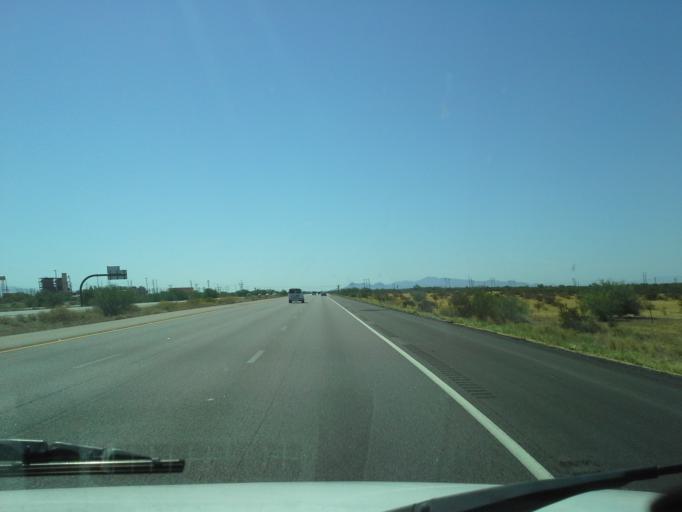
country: US
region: Arizona
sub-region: Pima County
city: Avra Valley
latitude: 32.5595
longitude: -111.3118
